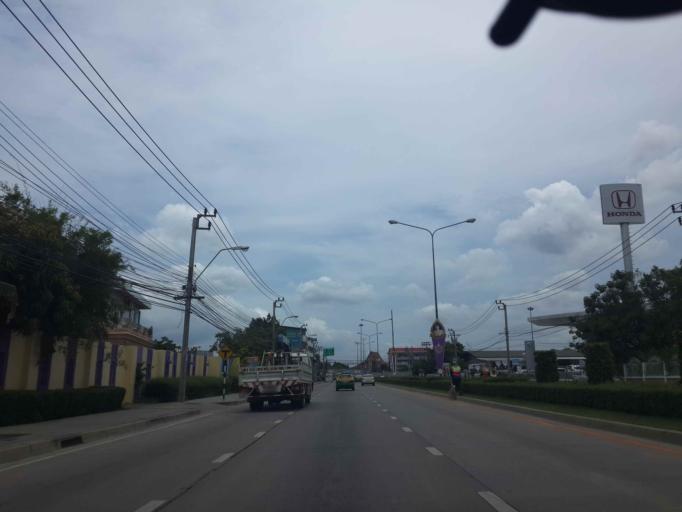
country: TH
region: Bangkok
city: Khan Na Yao
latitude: 13.8554
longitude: 100.6770
